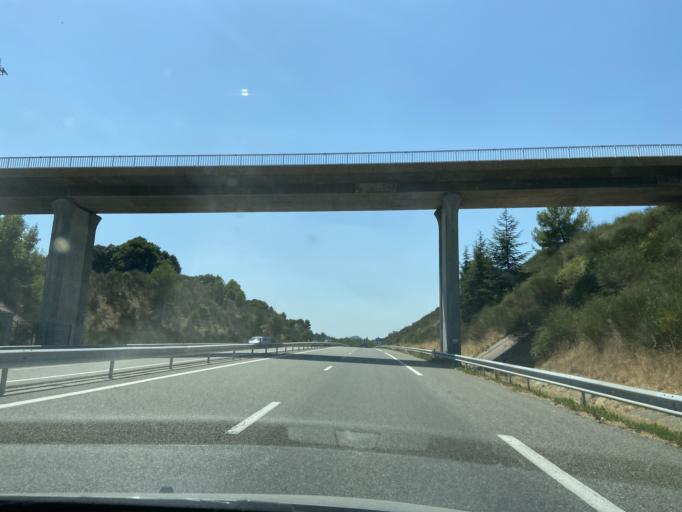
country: FR
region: Provence-Alpes-Cote d'Azur
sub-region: Departement des Alpes-de-Haute-Provence
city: Les Mees
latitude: 44.0658
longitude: 5.9670
